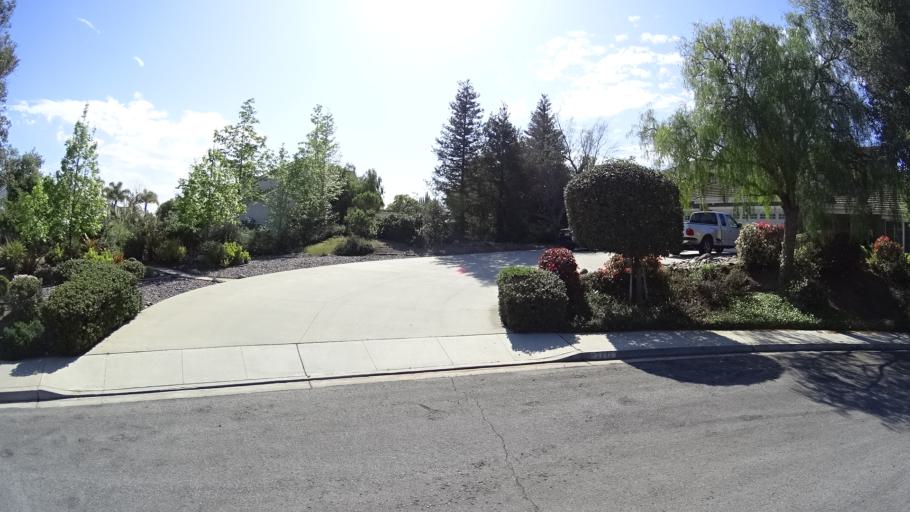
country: US
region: California
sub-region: Ventura County
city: Casa Conejo
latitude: 34.1741
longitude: -118.9249
